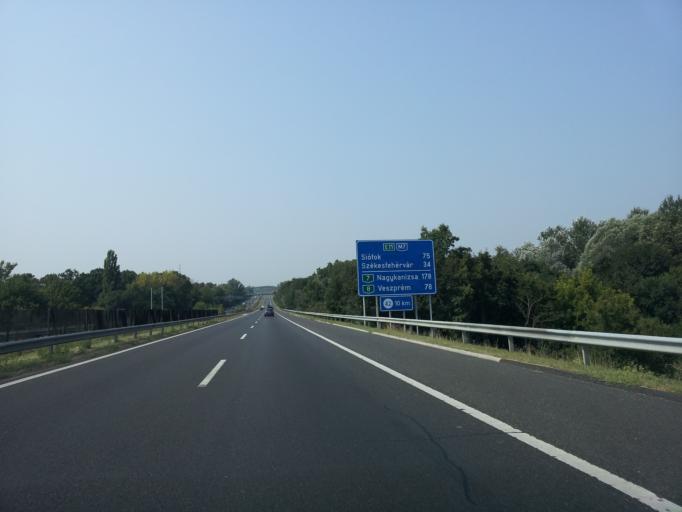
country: HU
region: Fejer
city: Martonvasar
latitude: 47.3260
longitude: 18.7701
